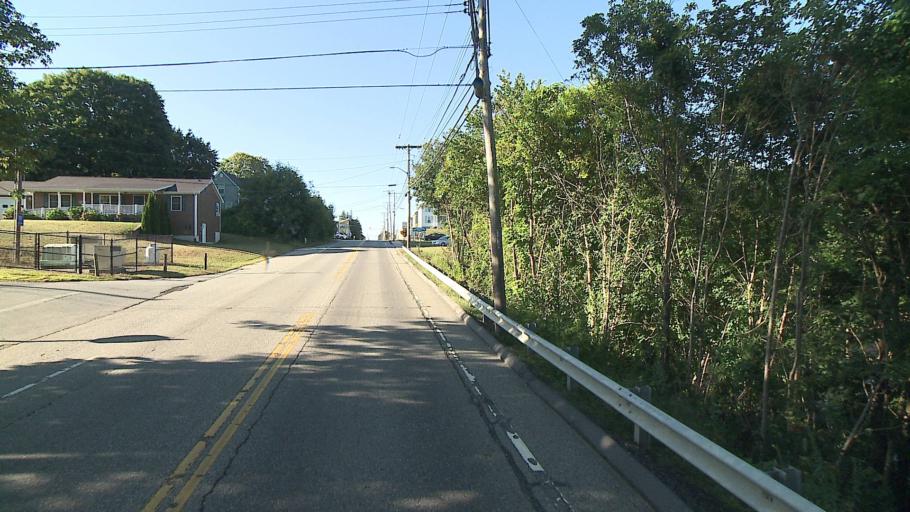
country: US
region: Connecticut
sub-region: New London County
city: Jewett City
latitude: 41.6152
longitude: -71.9790
